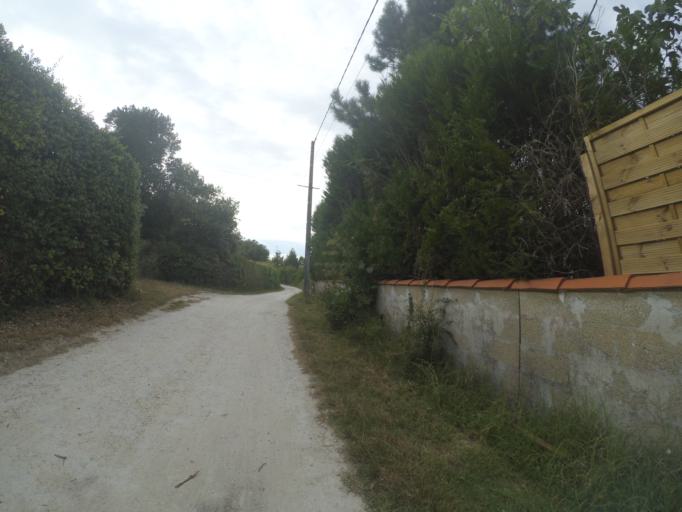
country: FR
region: Poitou-Charentes
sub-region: Departement de la Charente-Maritime
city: Meschers-sur-Gironde
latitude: 45.5726
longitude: -0.9665
